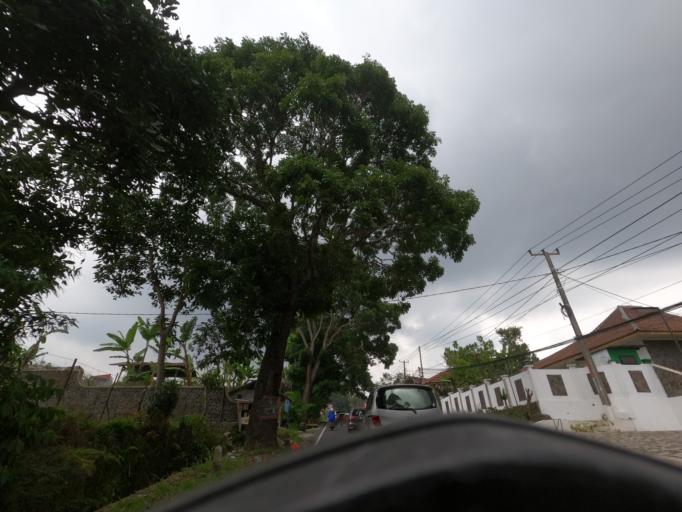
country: ID
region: West Java
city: Sukabumi
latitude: -6.7593
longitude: 107.0486
